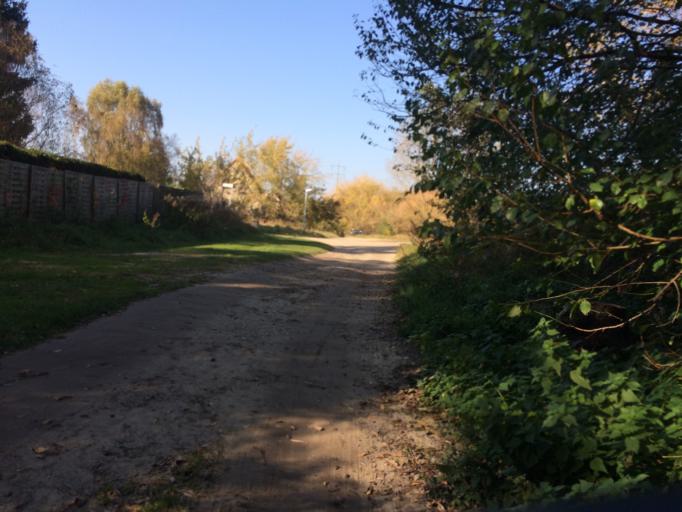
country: DE
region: Berlin
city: Blankenfelde
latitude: 52.6484
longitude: 13.3978
